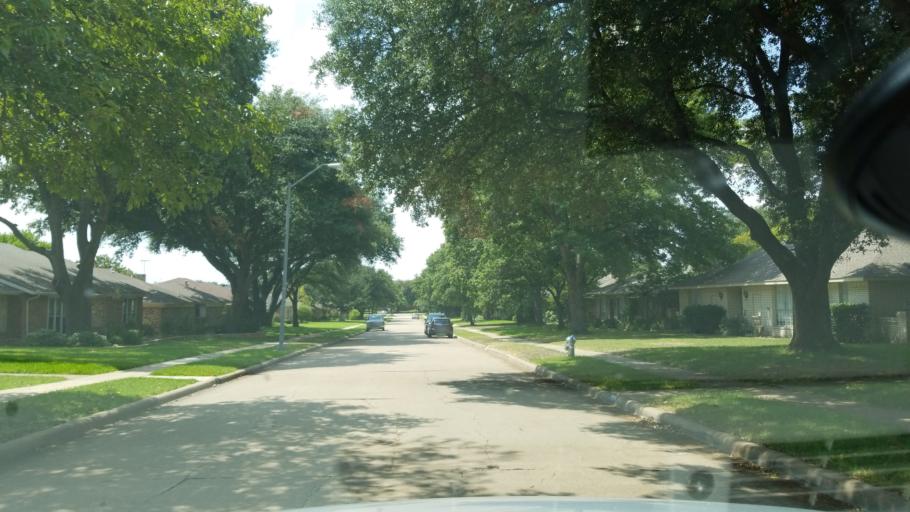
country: US
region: Texas
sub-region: Dallas County
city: Richardson
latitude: 32.9277
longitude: -96.7258
